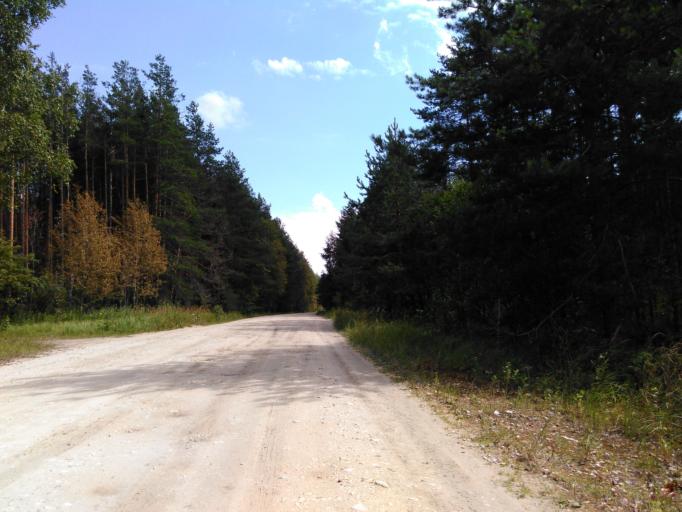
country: RU
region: Vladimir
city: Krasnyy Oktyabr'
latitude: 56.0058
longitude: 38.8338
